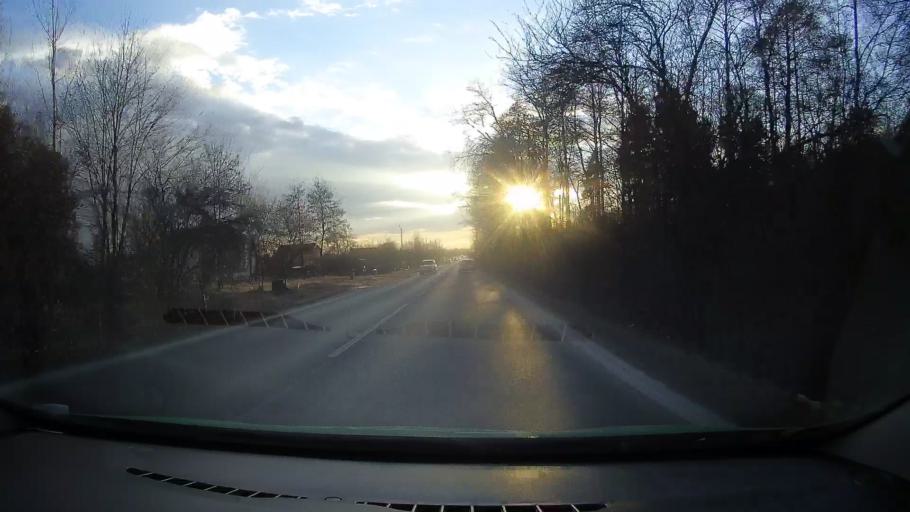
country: RO
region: Dambovita
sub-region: Comuna Gura Ocnitei
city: Adanca
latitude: 44.9096
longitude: 25.6317
